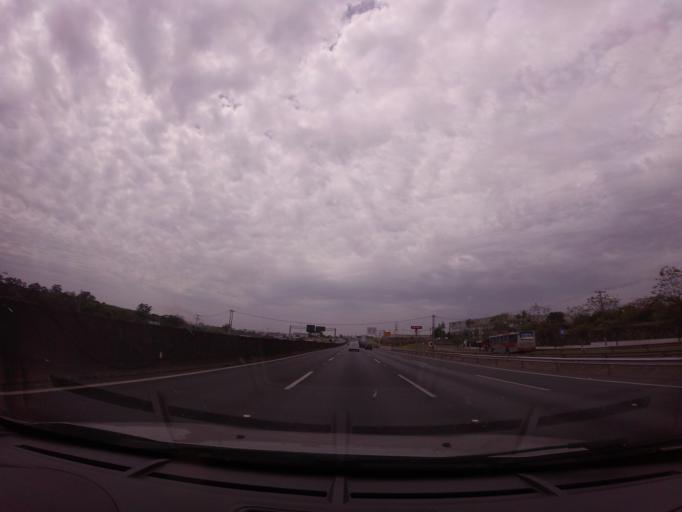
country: BR
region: Sao Paulo
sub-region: Hortolandia
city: Hortolandia
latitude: -22.8065
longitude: -47.2171
